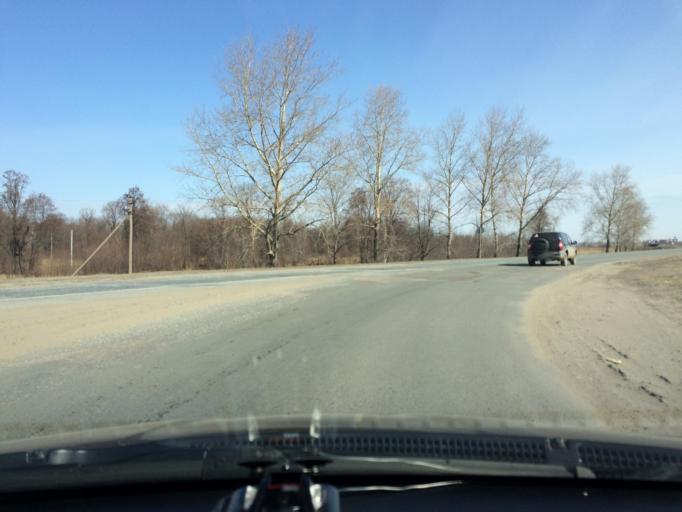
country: RU
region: Mariy-El
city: Yoshkar-Ola
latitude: 56.6461
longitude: 47.9372
